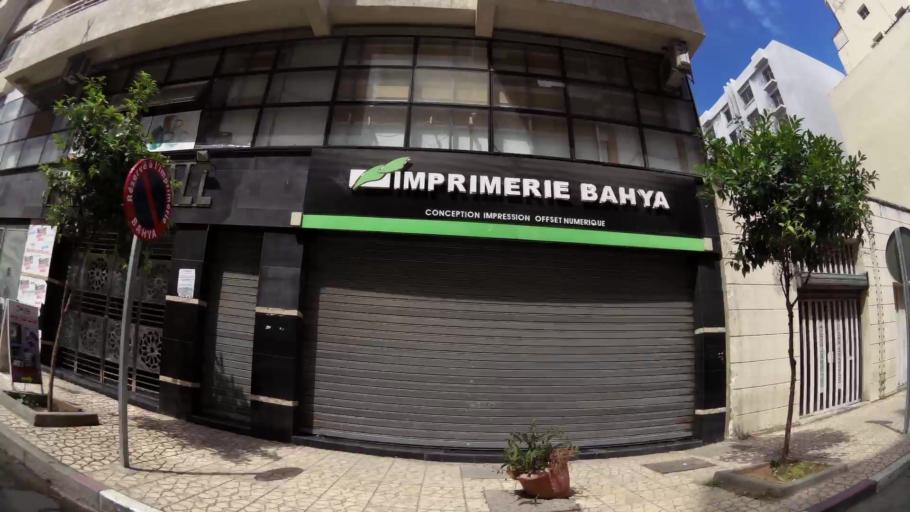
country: MA
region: Gharb-Chrarda-Beni Hssen
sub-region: Kenitra Province
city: Kenitra
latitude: 34.2595
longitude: -6.5832
